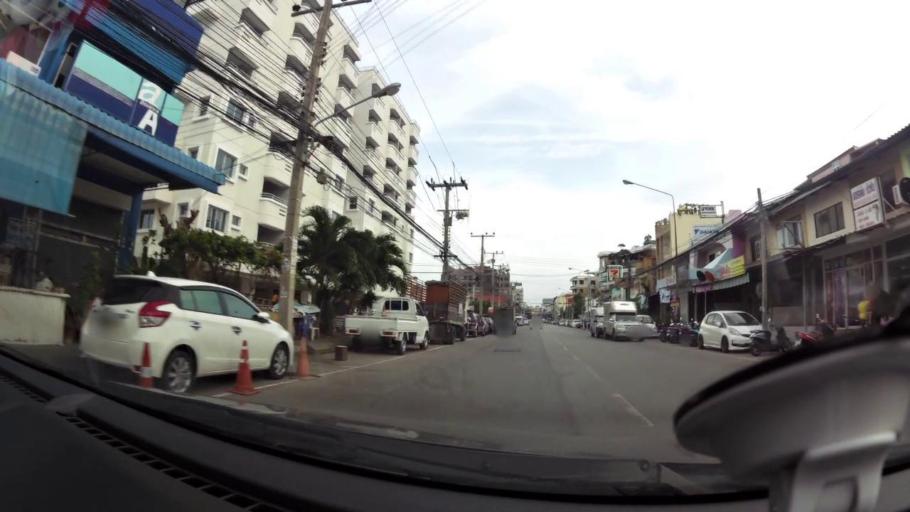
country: TH
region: Prachuap Khiri Khan
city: Hua Hin
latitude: 12.5751
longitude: 99.9568
